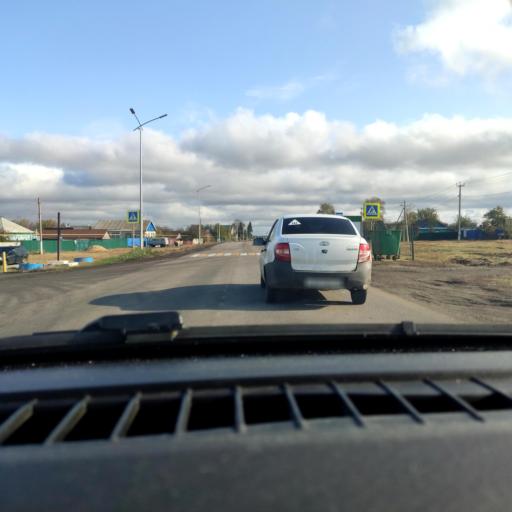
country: RU
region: Belgorod
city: Ilovka
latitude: 50.7316
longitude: 38.6932
